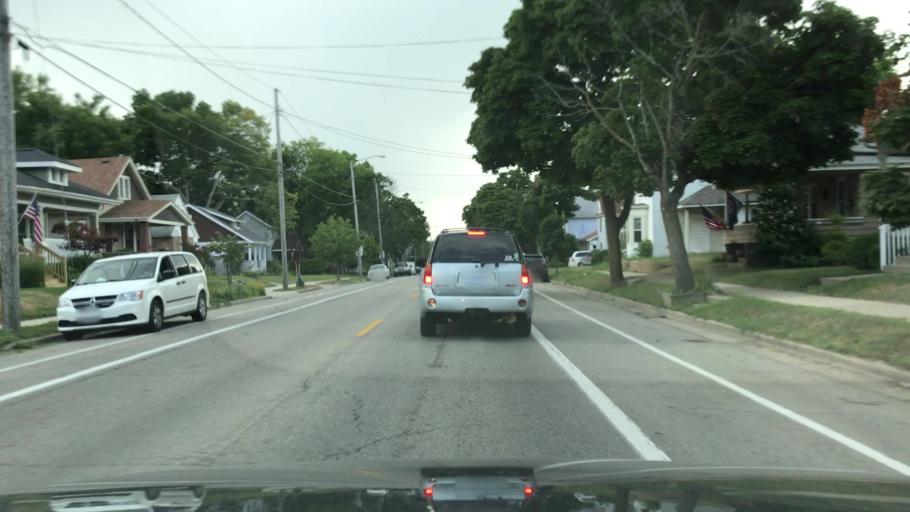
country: US
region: Michigan
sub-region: Kent County
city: Grand Rapids
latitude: 42.9955
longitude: -85.6653
